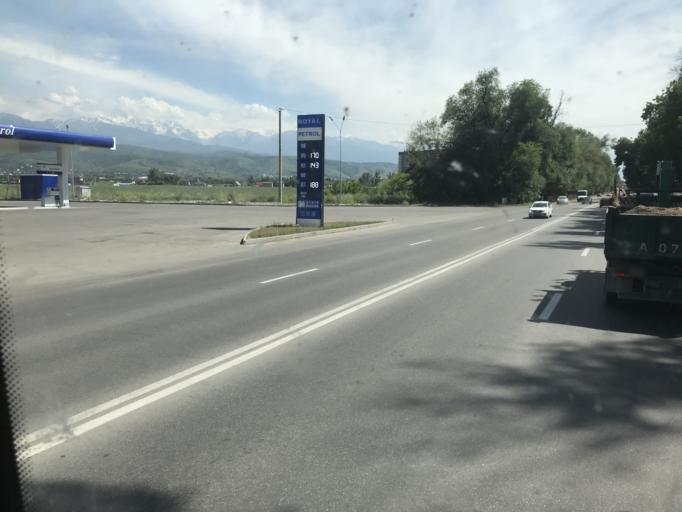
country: KZ
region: Almaty Oblysy
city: Energeticheskiy
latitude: 43.3284
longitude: 77.0329
